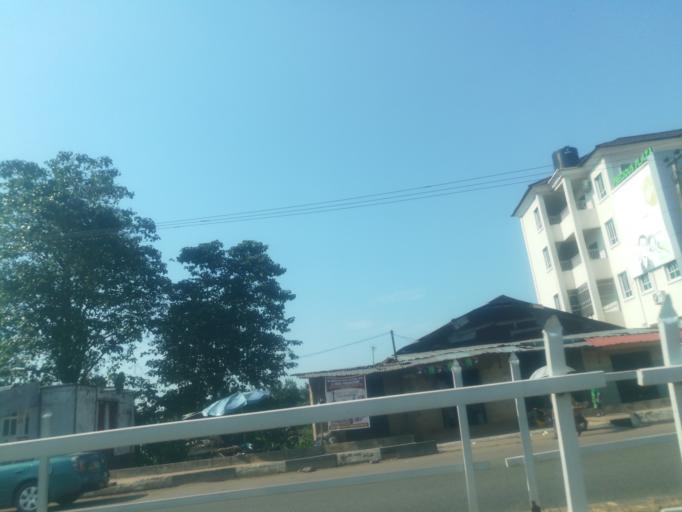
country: NG
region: Ogun
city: Abeokuta
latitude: 7.1392
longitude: 3.3357
